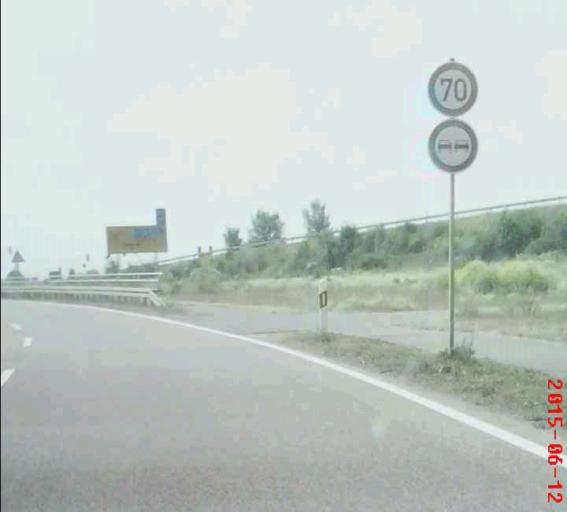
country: DE
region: Saxony-Anhalt
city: Bennungen
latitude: 51.4647
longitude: 11.0987
